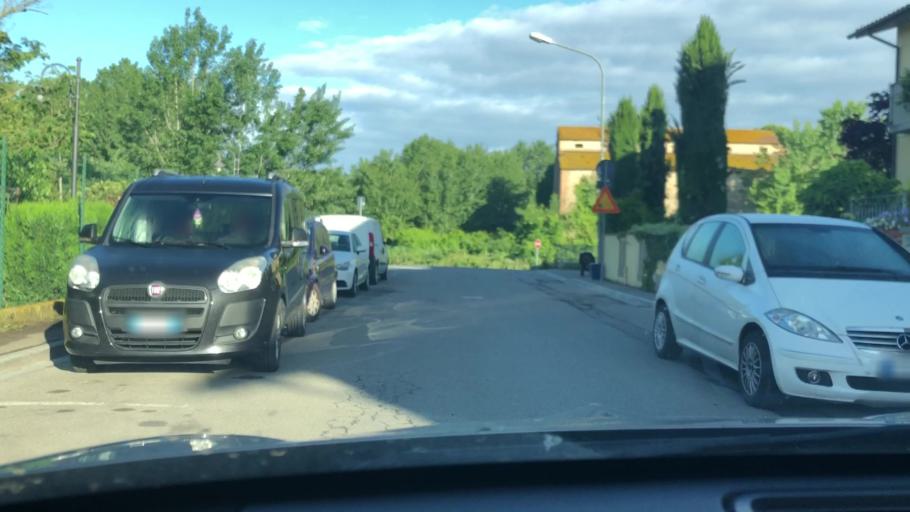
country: IT
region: Tuscany
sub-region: Province of Pisa
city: Forcoli
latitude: 43.6027
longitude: 10.7043
